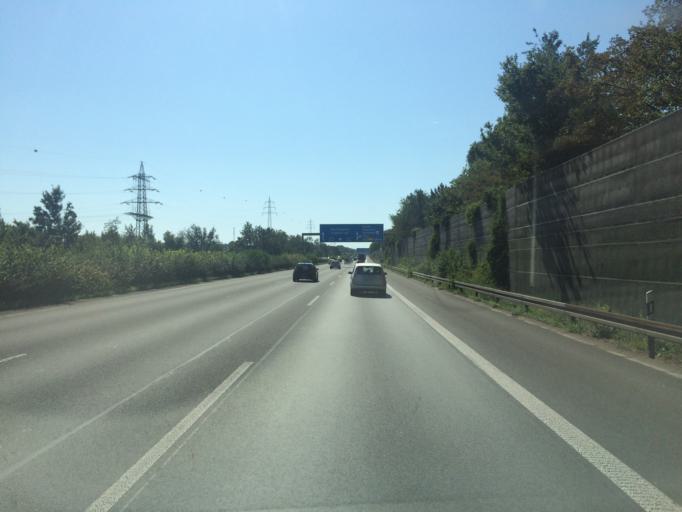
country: DE
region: North Rhine-Westphalia
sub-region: Regierungsbezirk Arnsberg
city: Unna
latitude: 51.5449
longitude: 7.6629
